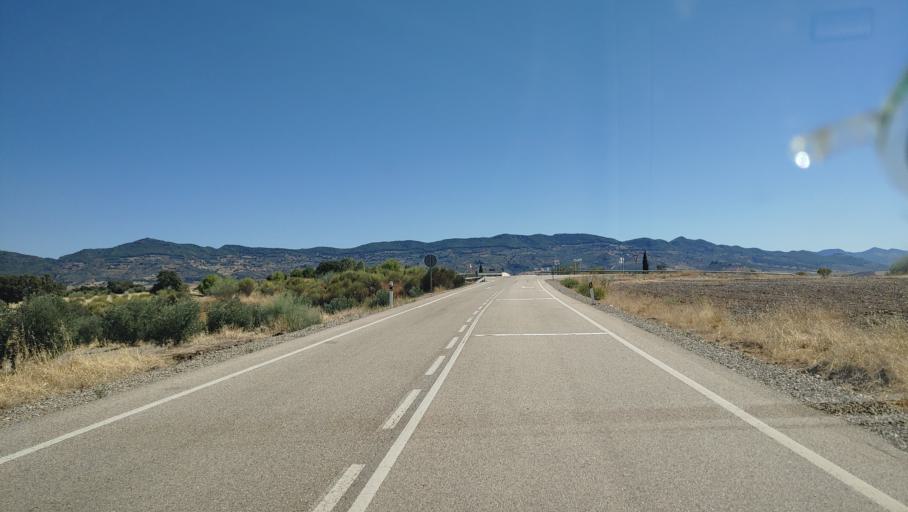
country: ES
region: Andalusia
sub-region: Provincia de Jaen
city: Genave
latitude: 38.4728
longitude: -2.7574
